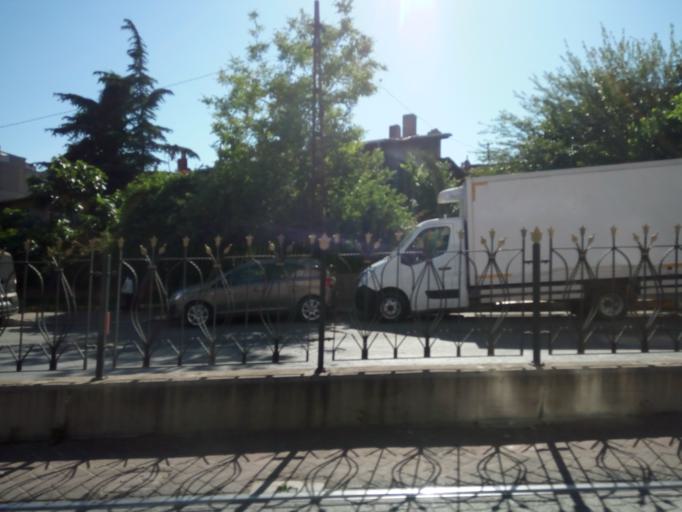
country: TR
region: Istanbul
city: Zeytinburnu
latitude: 41.0059
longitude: 28.9092
